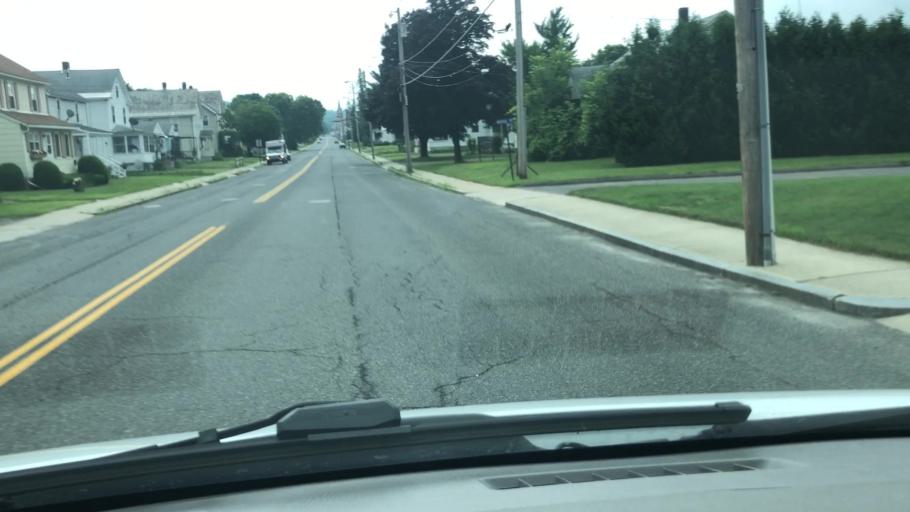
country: US
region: Massachusetts
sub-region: Berkshire County
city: Adams
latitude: 42.6328
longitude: -73.1100
